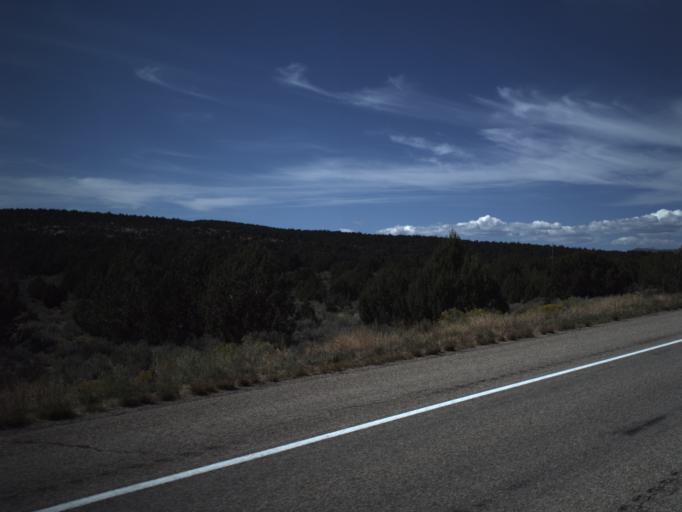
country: US
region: Utah
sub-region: Washington County
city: Ivins
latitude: 37.2731
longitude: -113.6440
